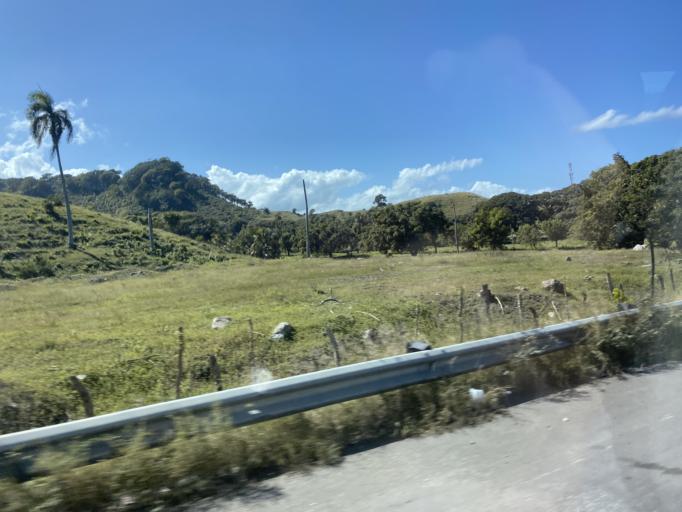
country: DO
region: Puerto Plata
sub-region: Puerto Plata
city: Puerto Plata
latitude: 19.8292
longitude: -70.7619
